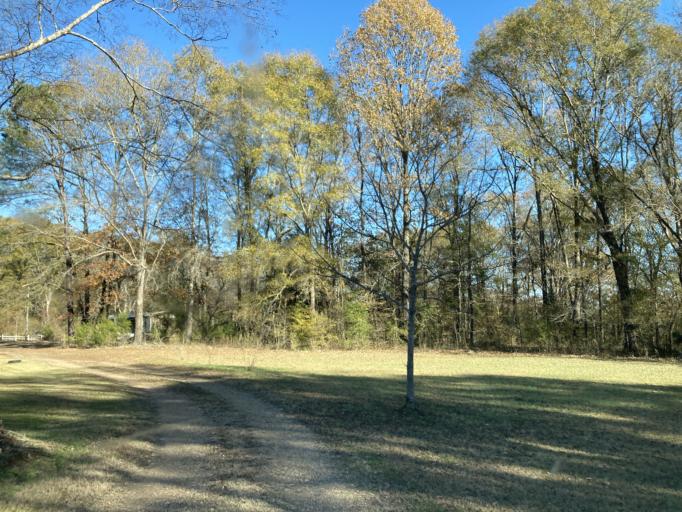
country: US
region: Mississippi
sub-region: Holmes County
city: Pickens
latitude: 32.8564
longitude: -90.0034
